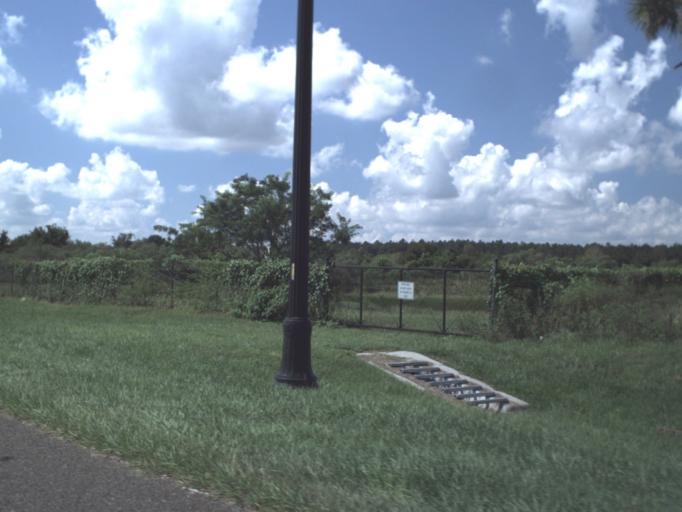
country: US
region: Florida
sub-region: Polk County
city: Haines City
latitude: 28.1322
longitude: -81.6398
